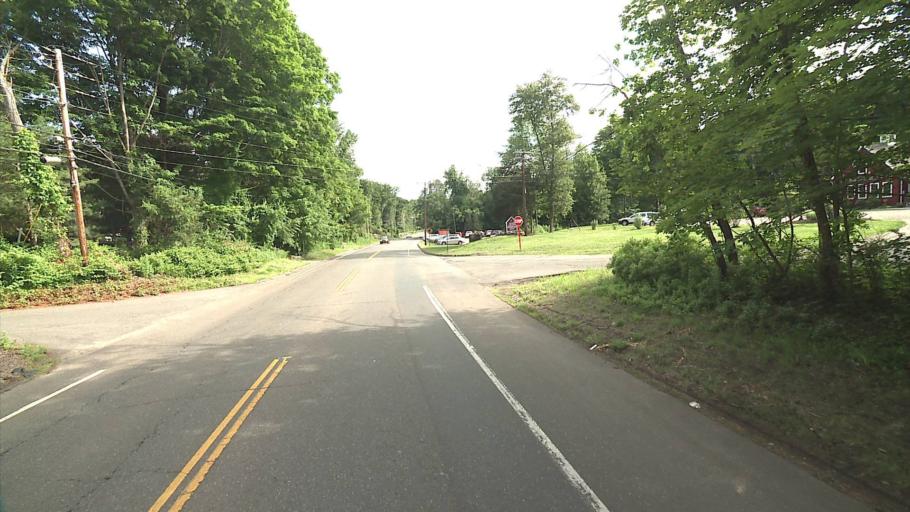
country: US
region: Connecticut
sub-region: New Haven County
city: Woodbridge
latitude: 41.4057
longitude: -73.0018
